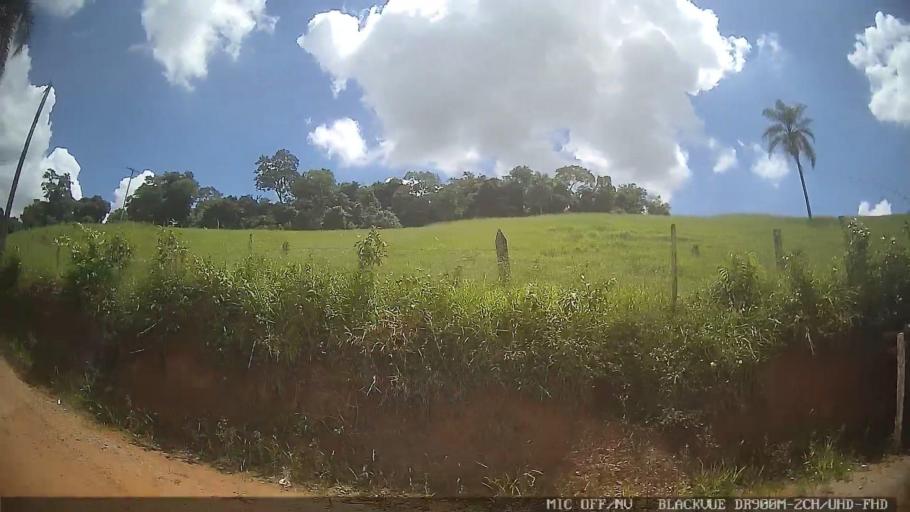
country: BR
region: Sao Paulo
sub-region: Jarinu
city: Jarinu
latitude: -23.1353
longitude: -46.6489
